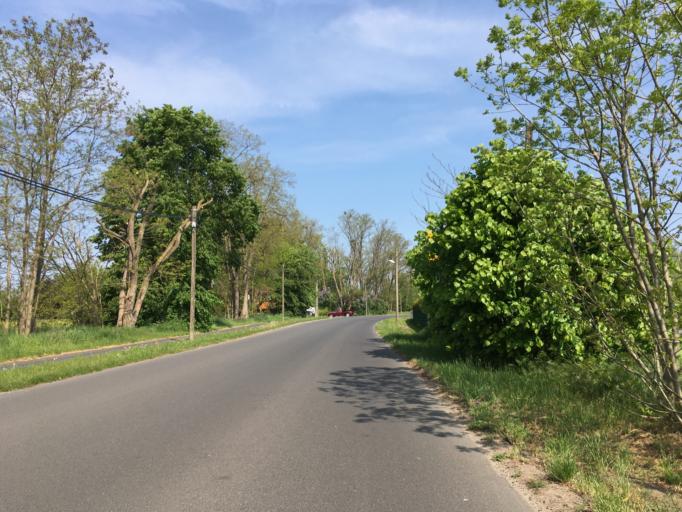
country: DE
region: Brandenburg
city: Altlandsberg
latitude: 52.5768
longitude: 13.7257
